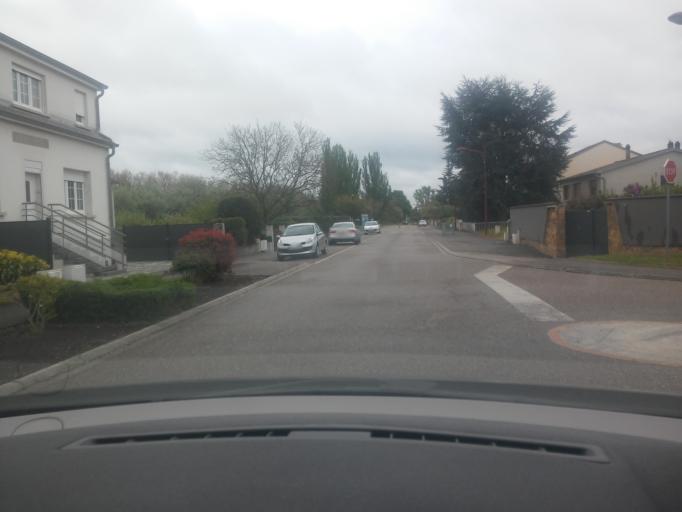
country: FR
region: Lorraine
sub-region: Departement de la Moselle
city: Ay-sur-Moselle
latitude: 49.2380
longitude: 6.2079
